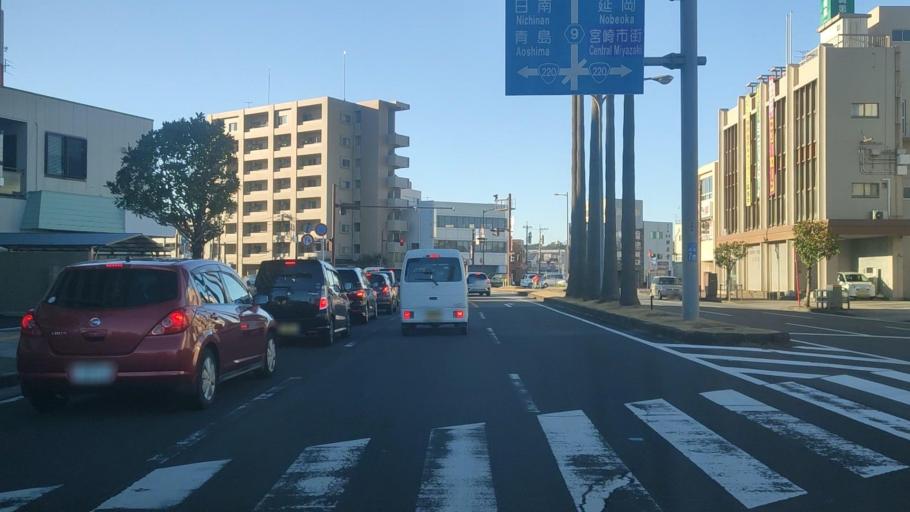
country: JP
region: Miyazaki
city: Miyazaki-shi
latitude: 31.8978
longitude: 131.4189
